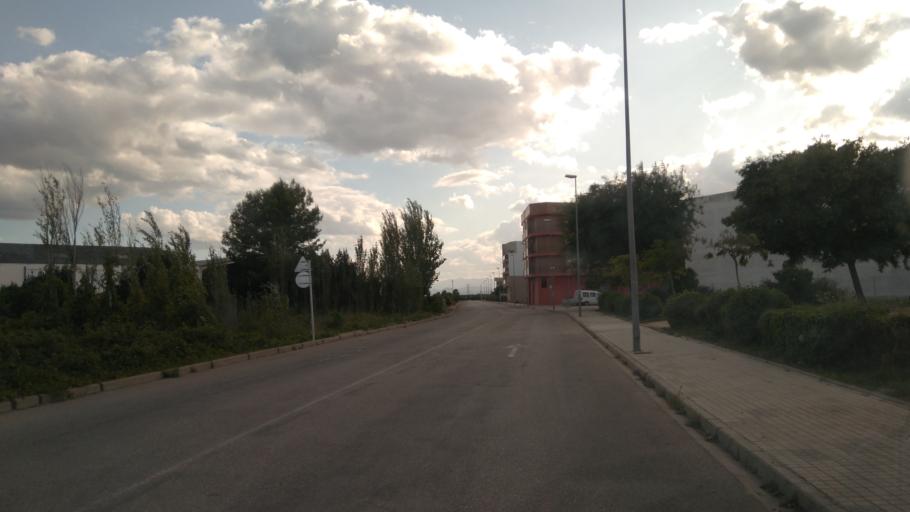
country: ES
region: Valencia
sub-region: Provincia de Valencia
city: L'Alcudia
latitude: 39.1953
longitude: -0.4991
